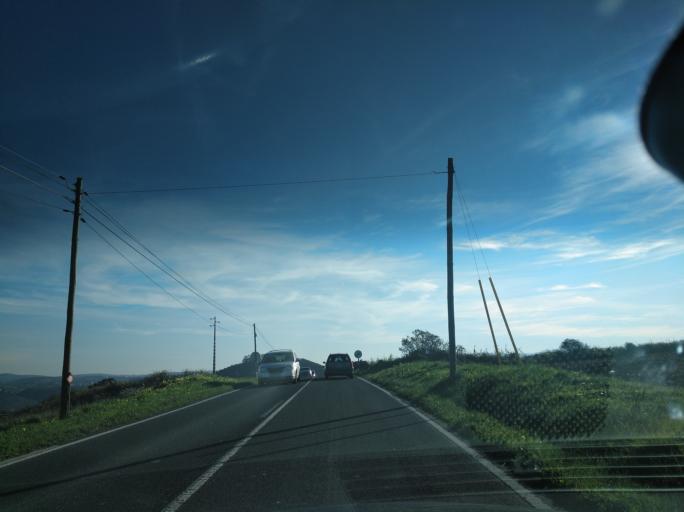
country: PT
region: Lisbon
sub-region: Mafra
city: Mafra
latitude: 38.9097
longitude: -9.3285
